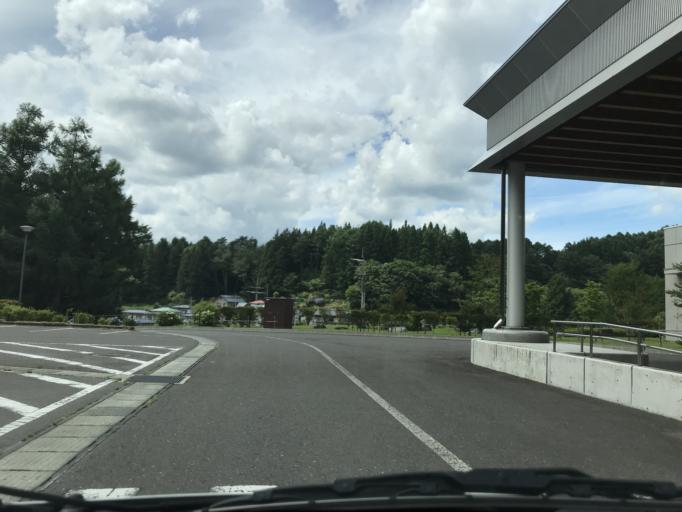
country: JP
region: Iwate
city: Tono
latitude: 39.3232
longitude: 141.5417
